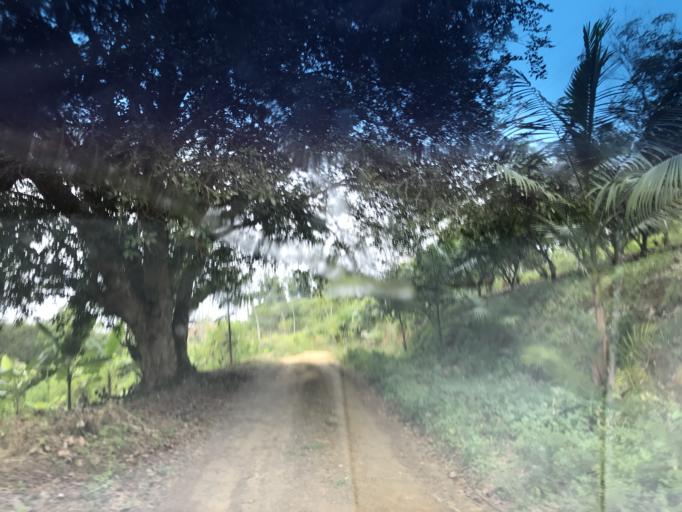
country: BR
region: Bahia
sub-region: Ibirapitanga
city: Ibirapitanga
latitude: -14.0478
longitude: -39.3574
